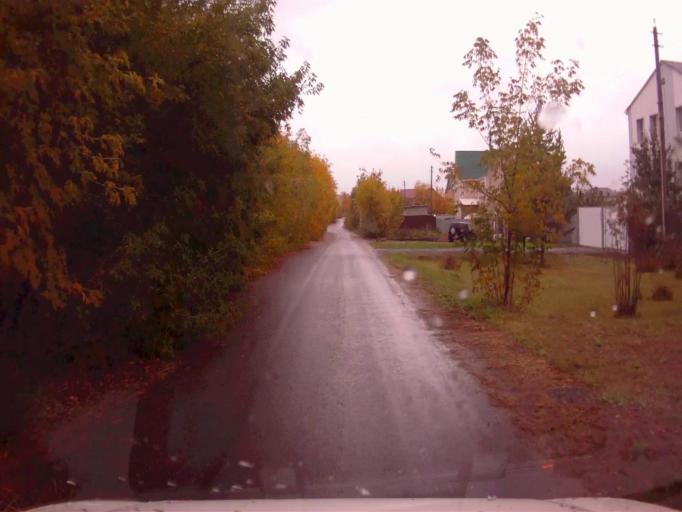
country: RU
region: Chelyabinsk
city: Dolgoderevenskoye
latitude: 55.3025
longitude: 61.3375
